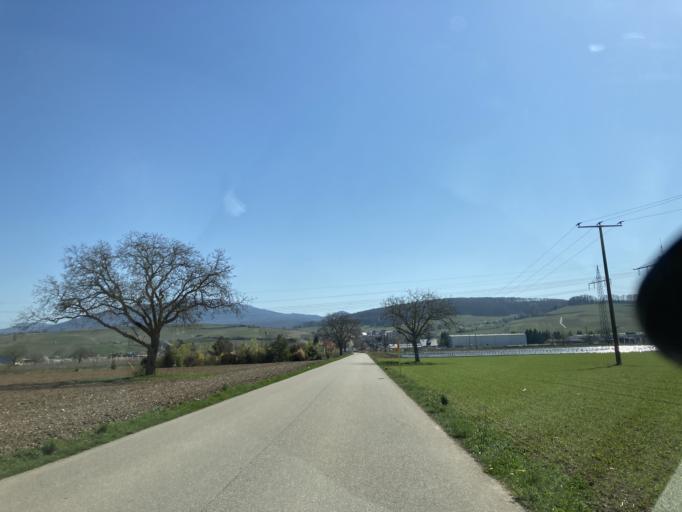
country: DE
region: Baden-Wuerttemberg
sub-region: Freiburg Region
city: Auggen
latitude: 47.7917
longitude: 7.5802
